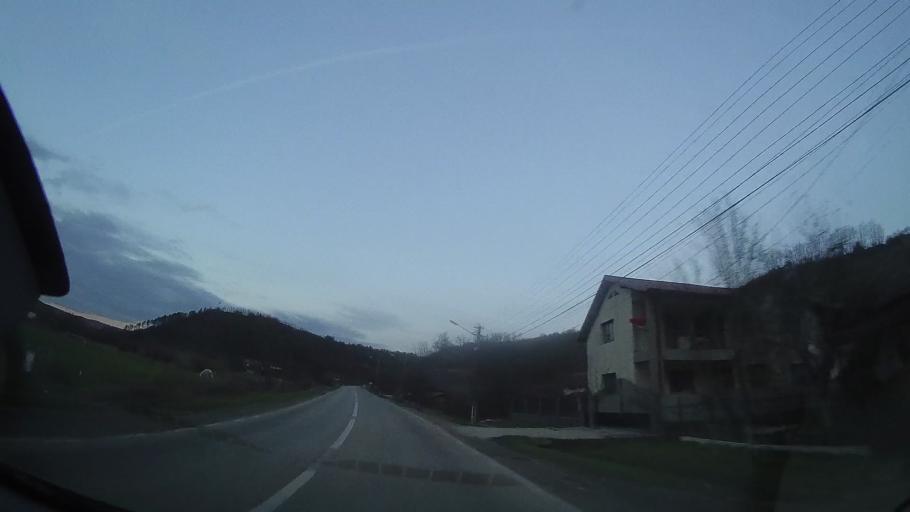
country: RO
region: Cluj
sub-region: Comuna Mociu
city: Mociu
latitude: 46.8010
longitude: 24.0406
